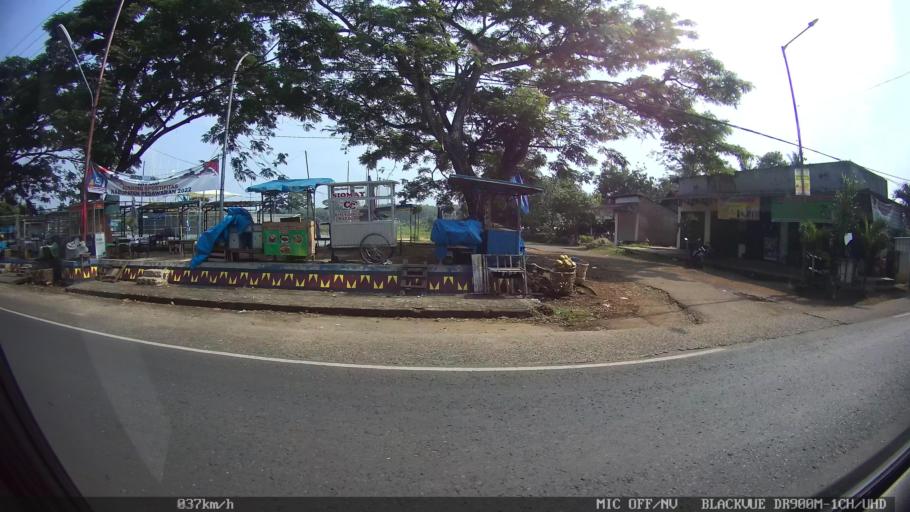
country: ID
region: Lampung
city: Gedongtataan
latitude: -5.3802
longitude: 105.1173
